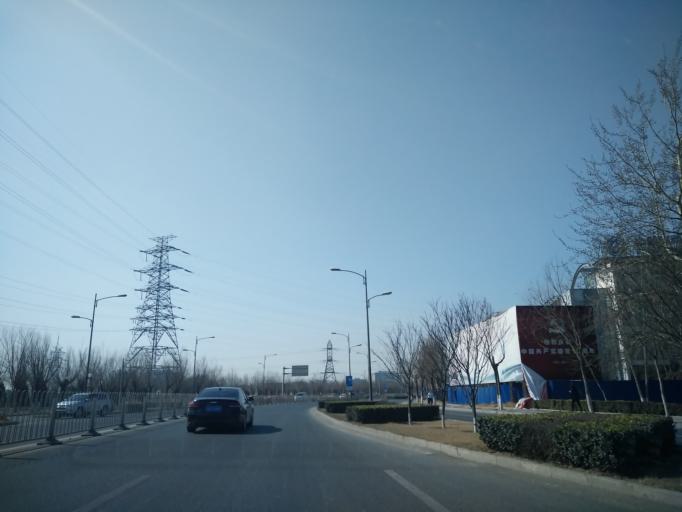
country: CN
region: Beijing
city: Qingyundian
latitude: 39.7629
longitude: 116.5361
